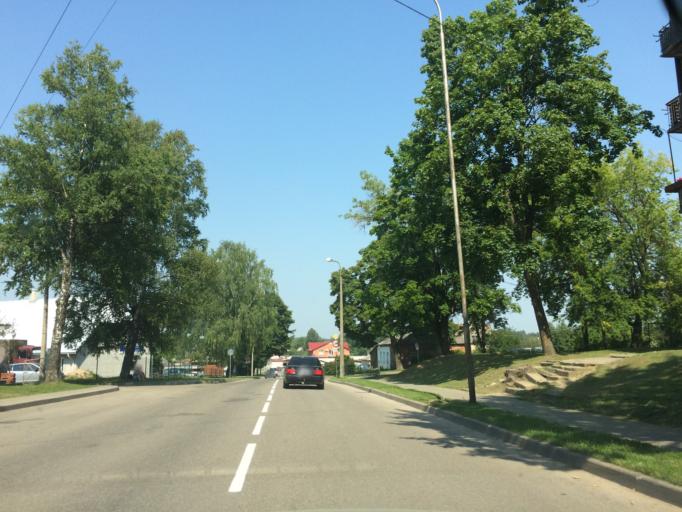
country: LV
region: Rezekne
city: Rezekne
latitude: 56.5103
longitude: 27.3258
